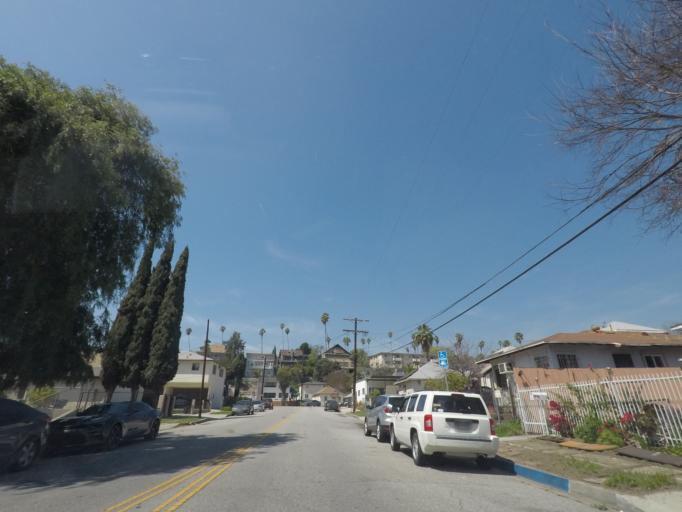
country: US
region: California
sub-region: Los Angeles County
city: South Pasadena
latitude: 34.1138
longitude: -118.1772
